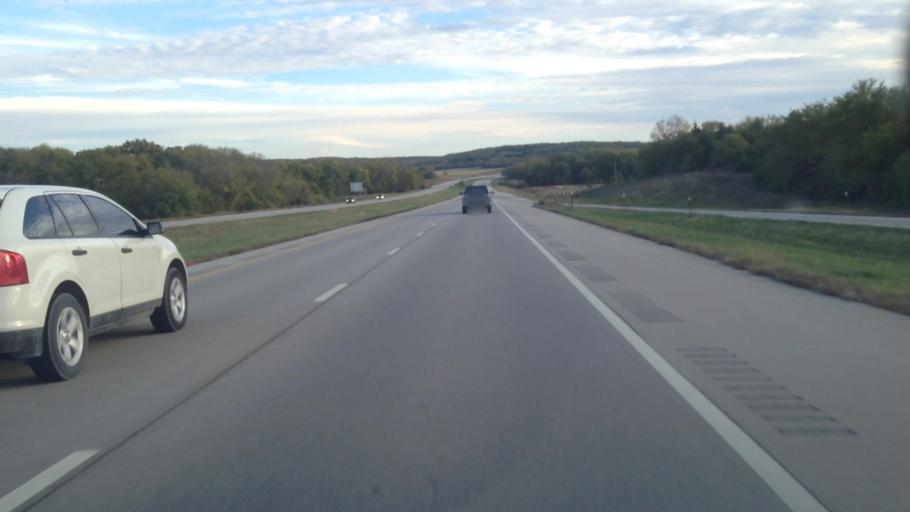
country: US
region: Kansas
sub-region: Douglas County
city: Lawrence
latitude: 38.8829
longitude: -95.2581
